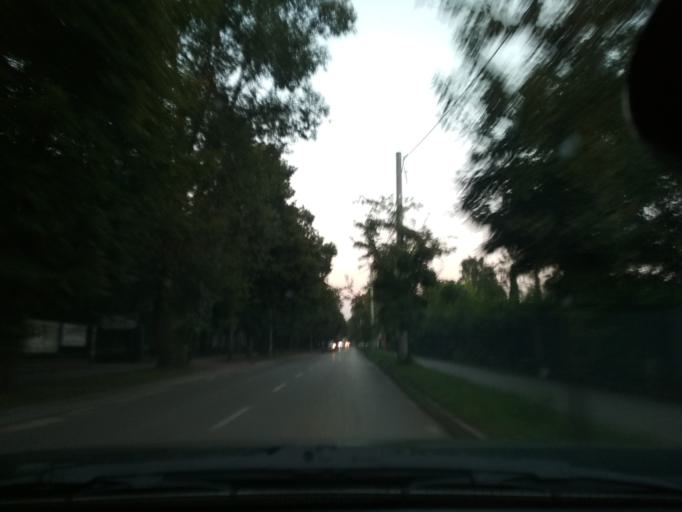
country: PL
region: Silesian Voivodeship
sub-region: Powiat zawiercianski
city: Zawiercie
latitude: 50.4872
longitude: 19.4293
